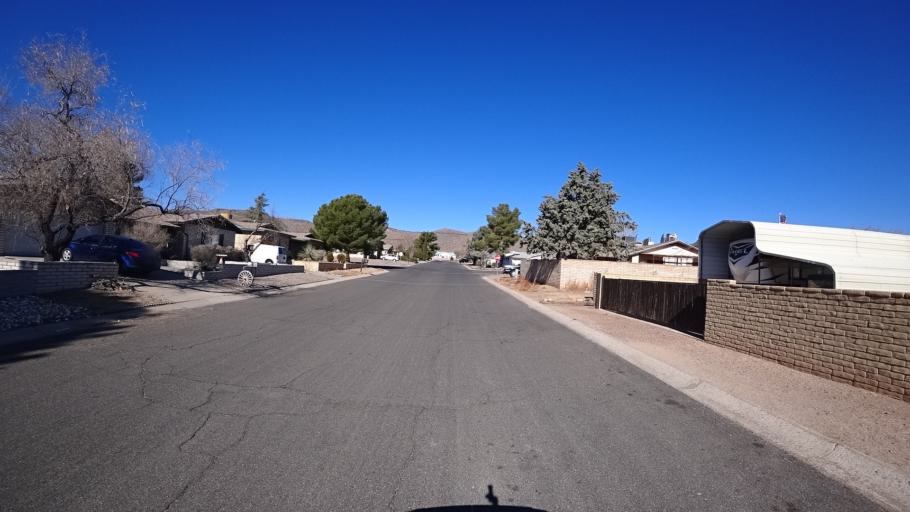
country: US
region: Arizona
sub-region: Mohave County
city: New Kingman-Butler
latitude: 35.2378
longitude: -114.0442
